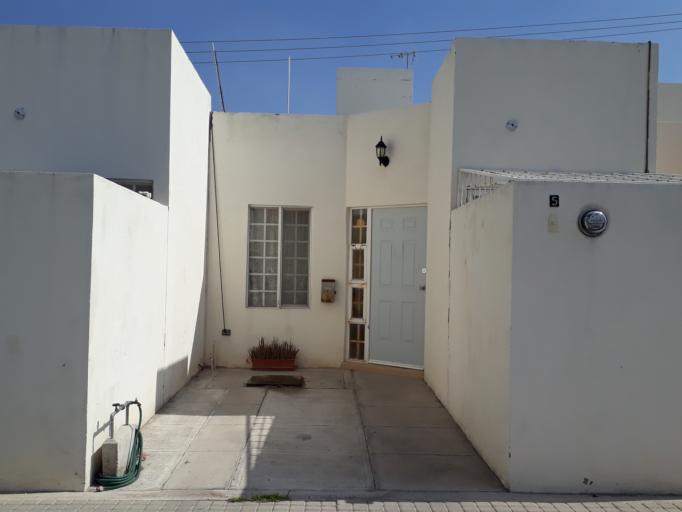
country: MX
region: Aguascalientes
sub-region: Aguascalientes
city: San Sebastian [Fraccionamiento]
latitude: 21.8082
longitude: -102.2940
